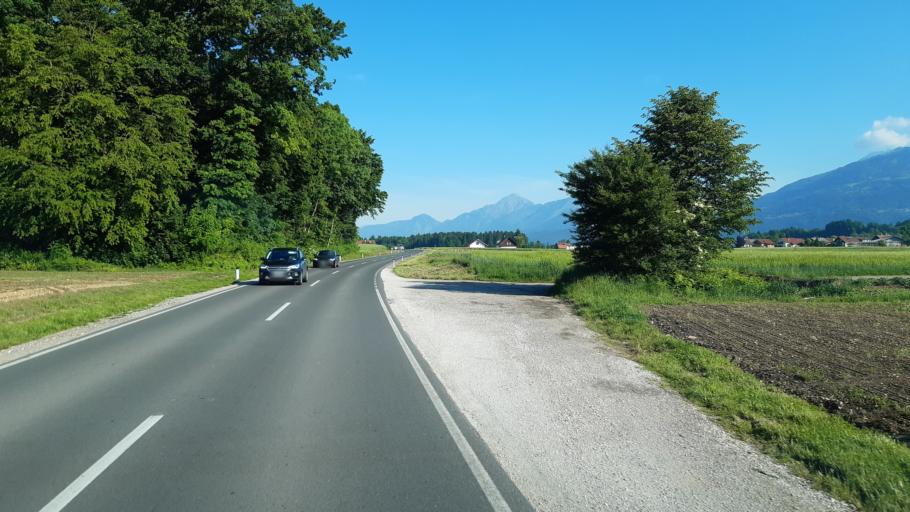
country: SI
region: Komenda
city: Komenda
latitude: 46.1977
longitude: 14.5398
